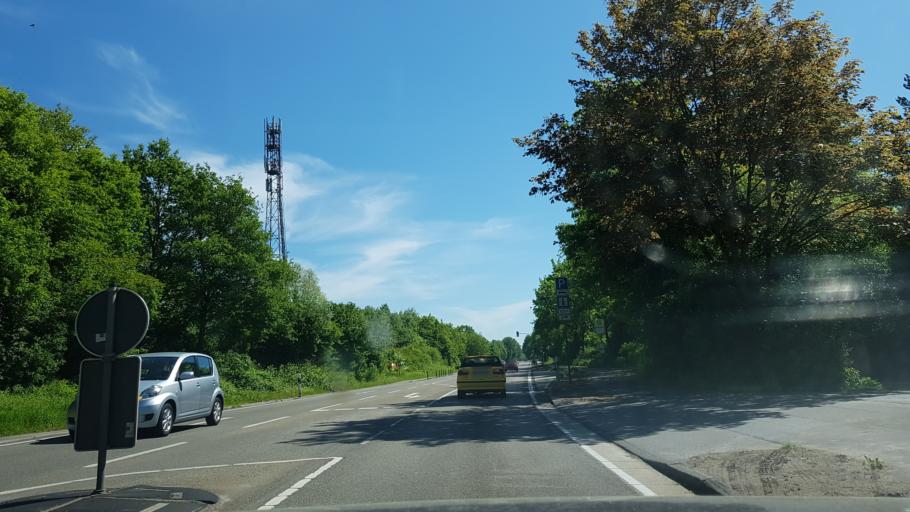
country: DE
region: North Rhine-Westphalia
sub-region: Regierungsbezirk Dusseldorf
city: Ratingen
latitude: 51.2959
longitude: 6.8932
